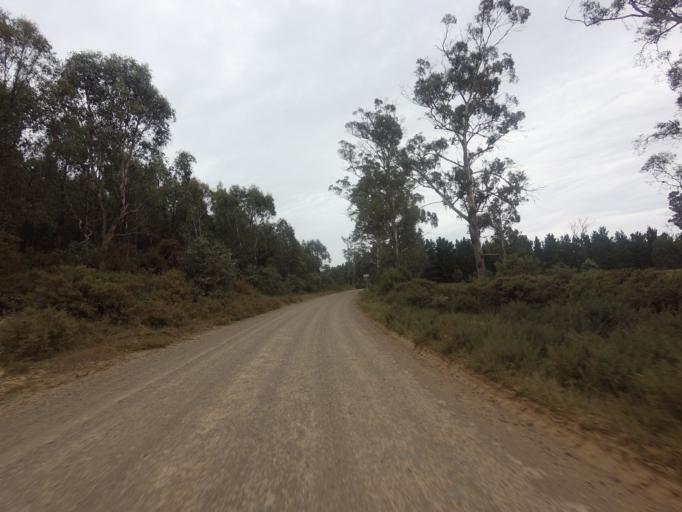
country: AU
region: Tasmania
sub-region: Derwent Valley
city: New Norfolk
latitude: -42.5768
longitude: 147.0015
